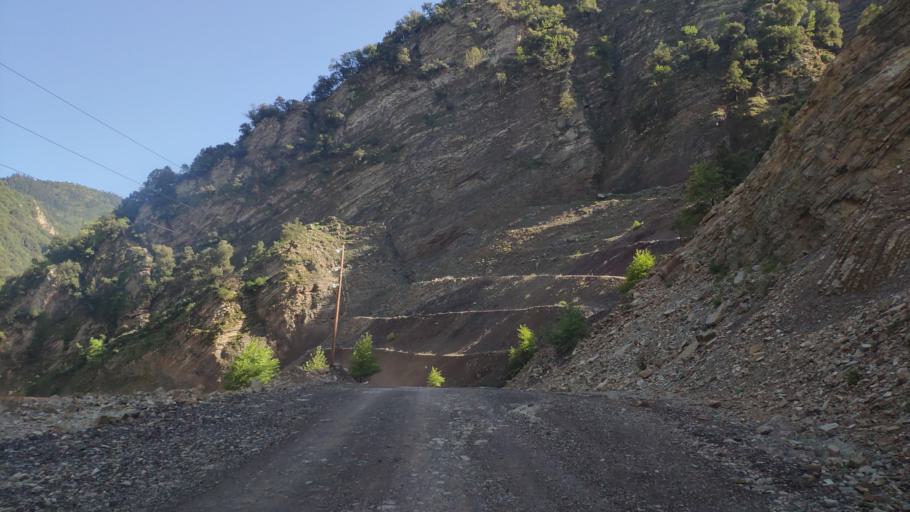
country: GR
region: Central Greece
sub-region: Nomos Evrytanias
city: Kerasochori
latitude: 39.0718
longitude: 21.6013
